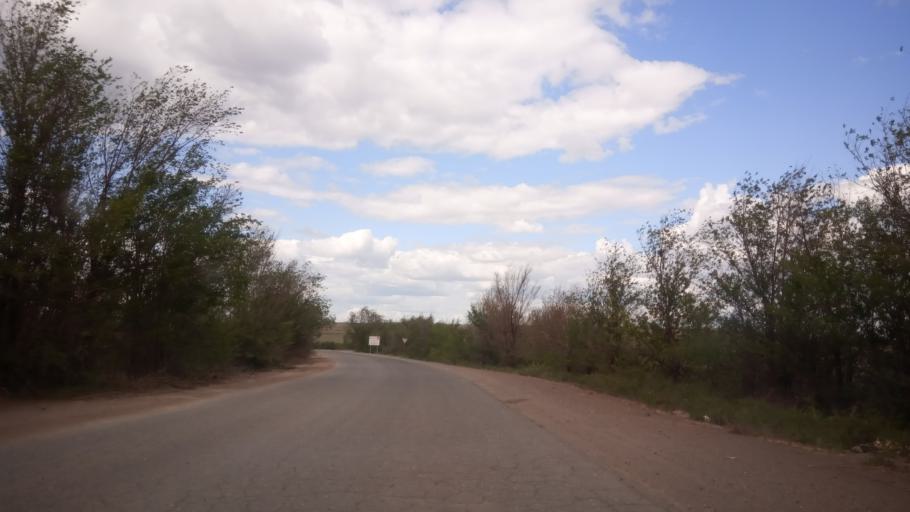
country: RU
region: Orenburg
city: Novotroitsk
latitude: 51.2517
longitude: 58.3659
